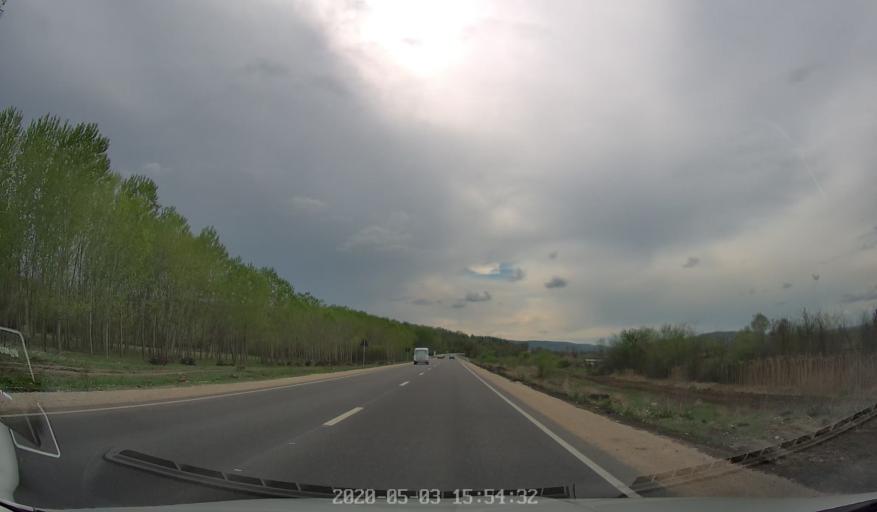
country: MD
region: Stinga Nistrului
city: Bucovat
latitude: 47.1772
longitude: 28.4947
